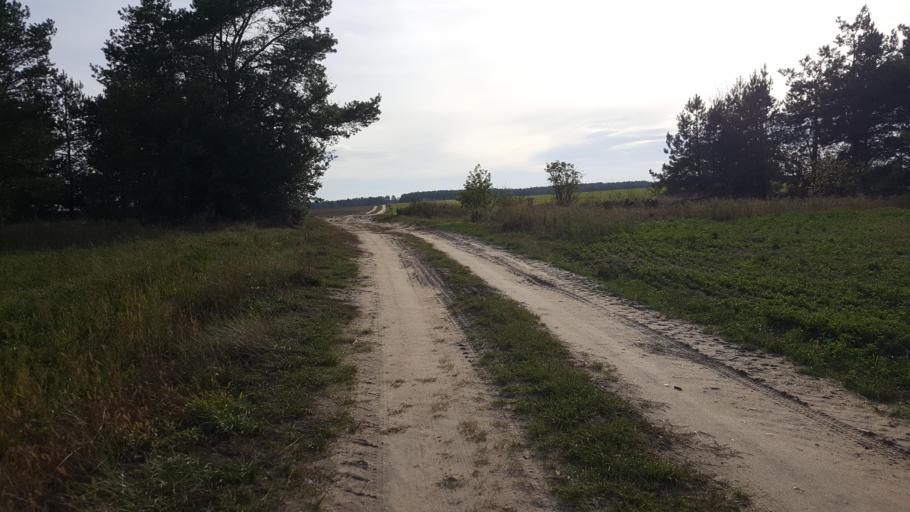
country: BY
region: Brest
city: Kamyanyets
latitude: 52.3981
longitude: 23.8552
